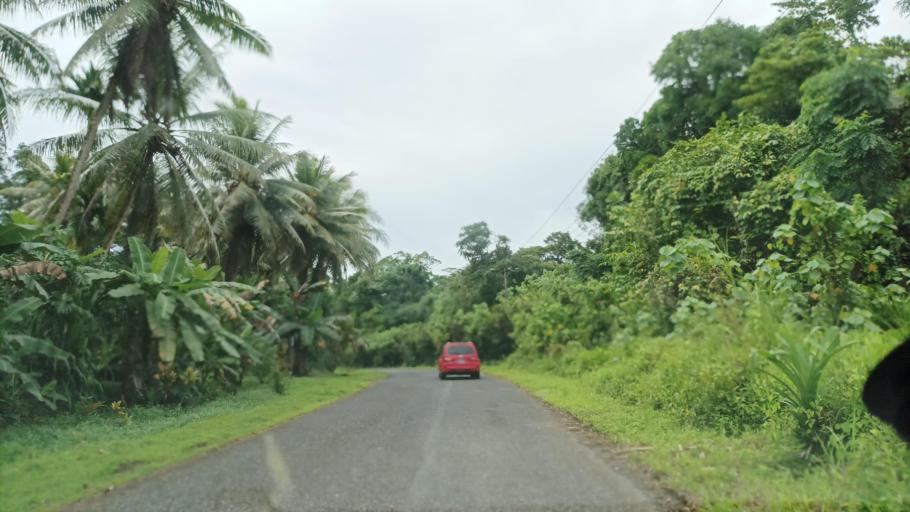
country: FM
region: Pohnpei
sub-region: Madolenihm Municipality
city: Madolenihm Municipality Government
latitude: 6.8967
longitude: 158.3137
